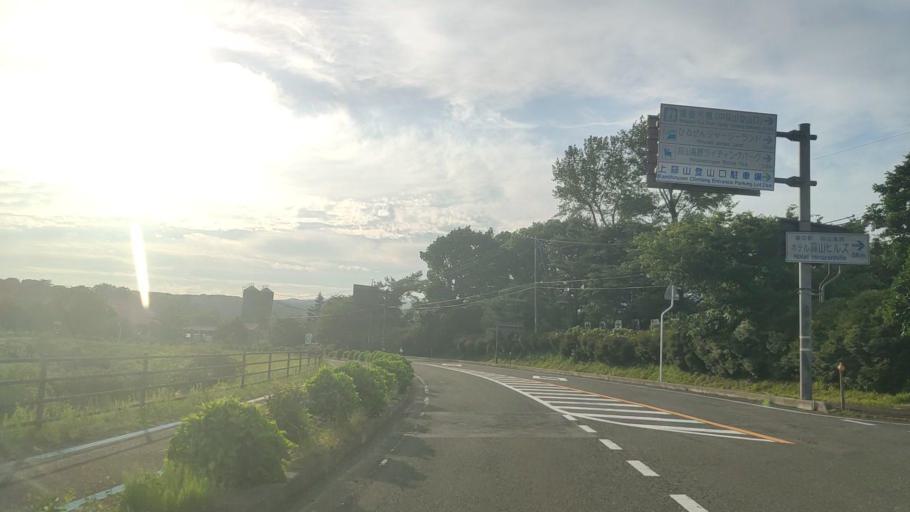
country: JP
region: Tottori
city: Kurayoshi
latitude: 35.2986
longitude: 133.6322
